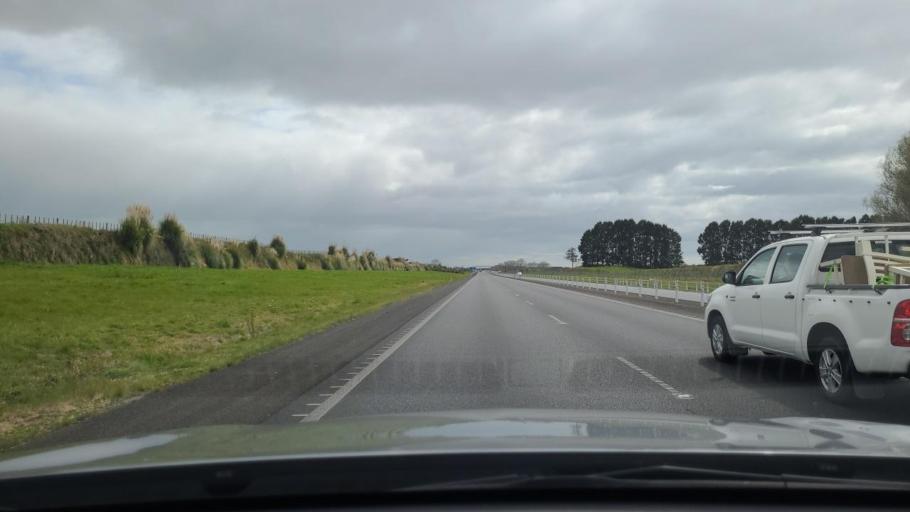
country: NZ
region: Bay of Plenty
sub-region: Western Bay of Plenty District
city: Maketu
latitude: -37.7837
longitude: 176.3885
